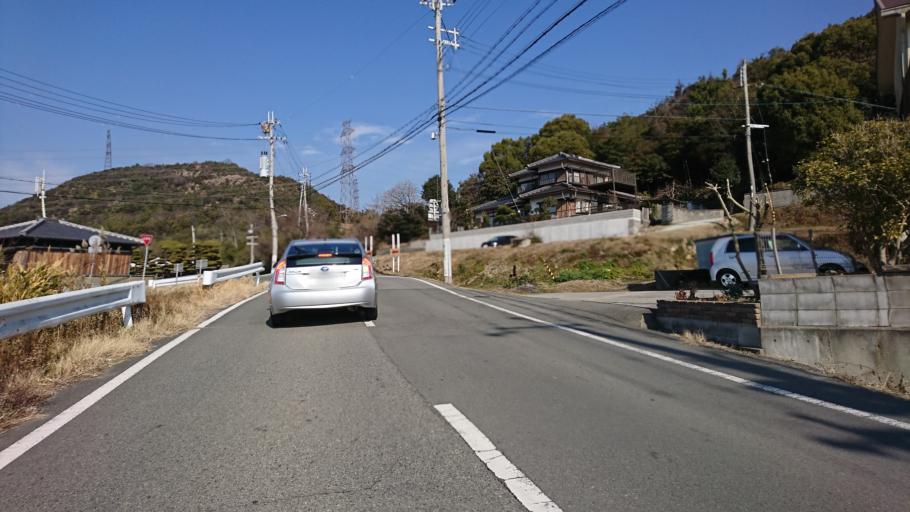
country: JP
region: Hyogo
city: Kakogawacho-honmachi
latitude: 34.7958
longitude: 134.8395
